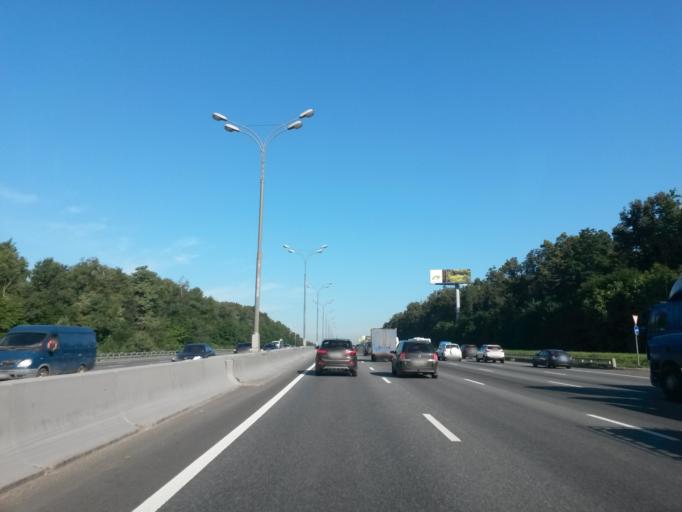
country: RU
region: Moscow
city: Gol'yanovo
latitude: 55.8362
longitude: 37.8161
